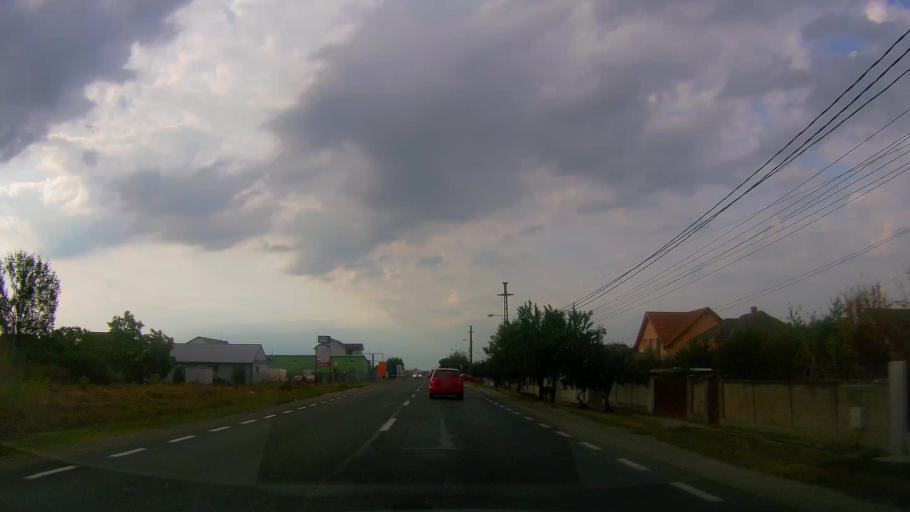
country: RO
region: Satu Mare
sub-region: Comuna Paulesti
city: Paulesti
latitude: 47.7568
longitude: 22.8833
